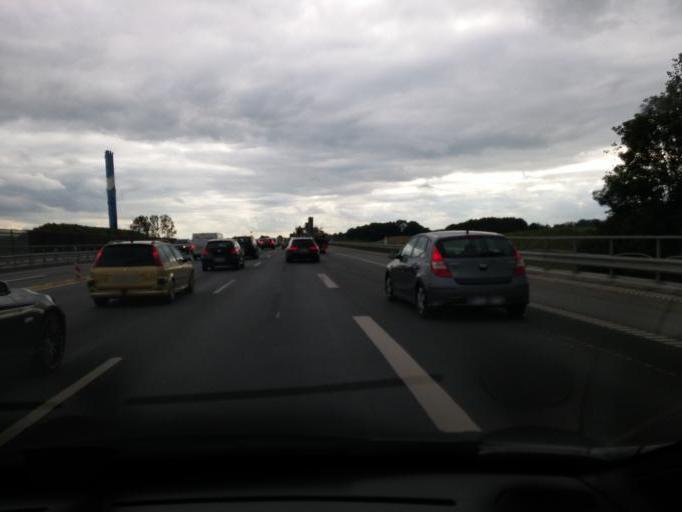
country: DK
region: Zealand
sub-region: Solrod Kommune
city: Solrod Strand
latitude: 55.5433
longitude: 12.2124
